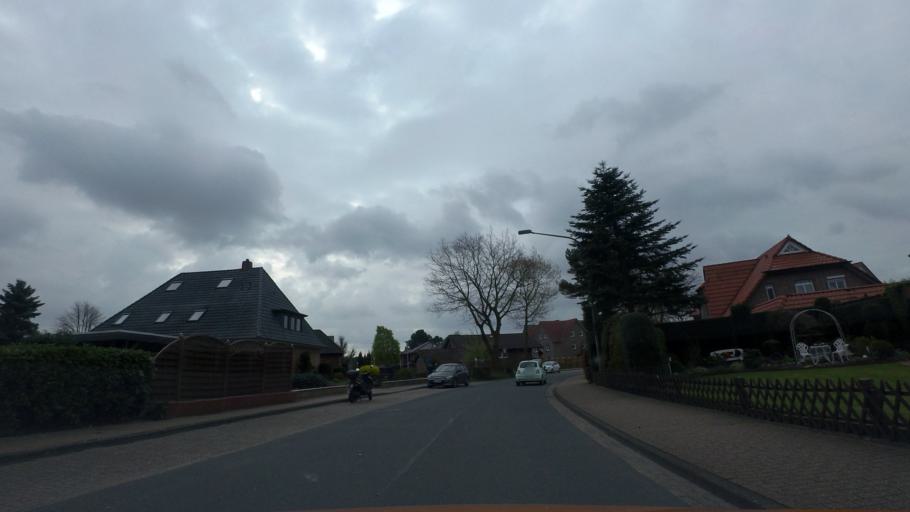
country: DE
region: Lower Saxony
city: Wardenburg
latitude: 53.0619
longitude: 8.2005
